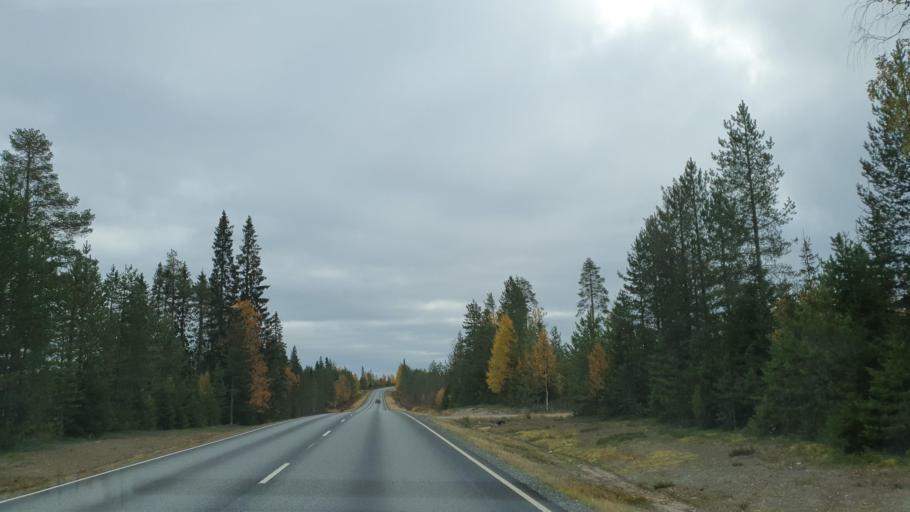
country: FI
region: Lapland
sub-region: Rovaniemi
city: Ranua
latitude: 65.8063
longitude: 26.5621
